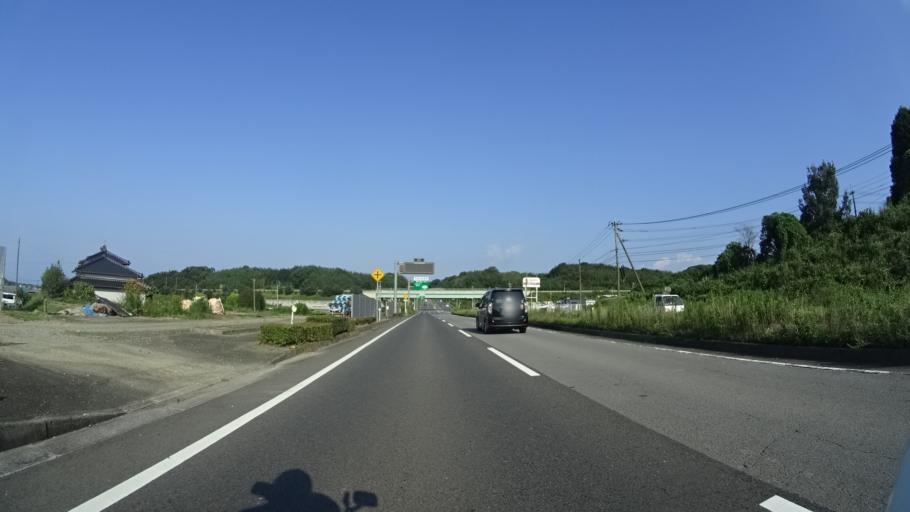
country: JP
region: Fukuoka
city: Nakatsu
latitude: 33.5530
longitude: 131.2420
